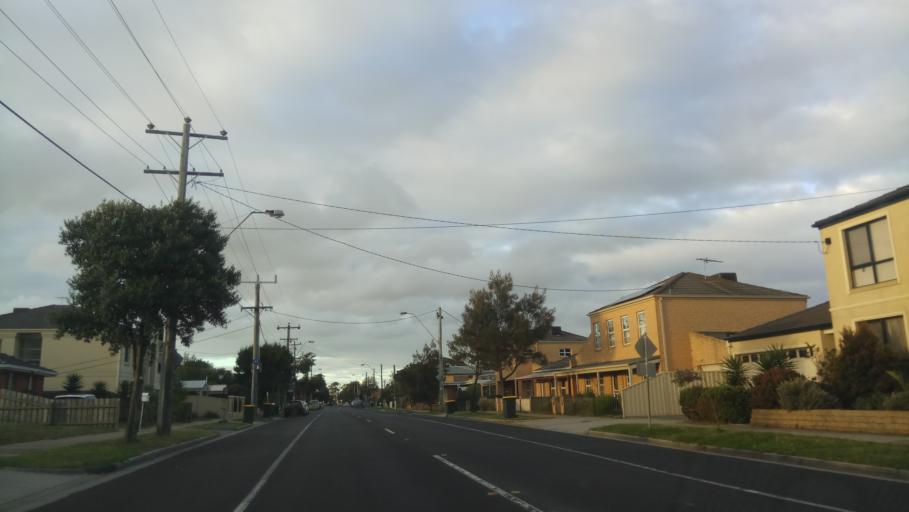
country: AU
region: Victoria
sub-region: Hobsons Bay
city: Altona
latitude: -37.8701
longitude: 144.8383
